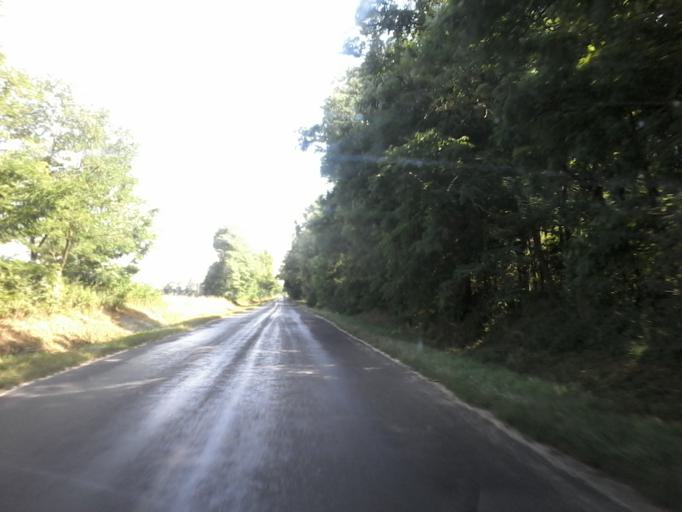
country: HU
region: Zala
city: Turje
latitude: 47.0562
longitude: 17.1252
